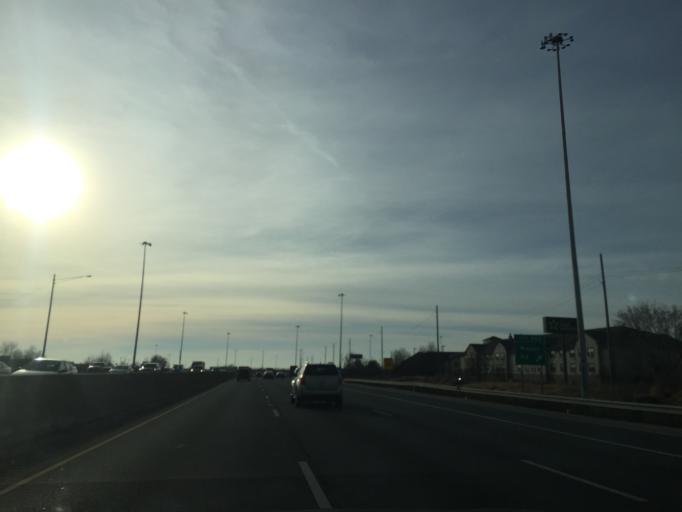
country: US
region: Illinois
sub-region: Will County
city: Romeoville
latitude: 41.6586
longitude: -88.1182
